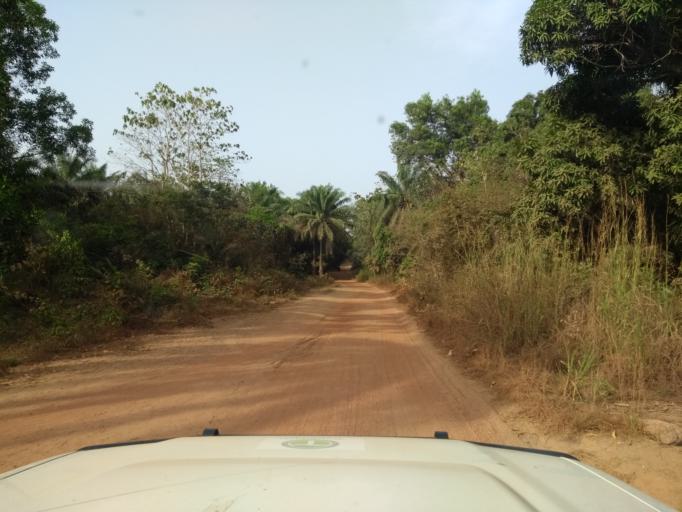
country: GN
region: Kindia
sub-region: Prefecture de Dubreka
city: Dubreka
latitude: 9.8559
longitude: -13.5495
